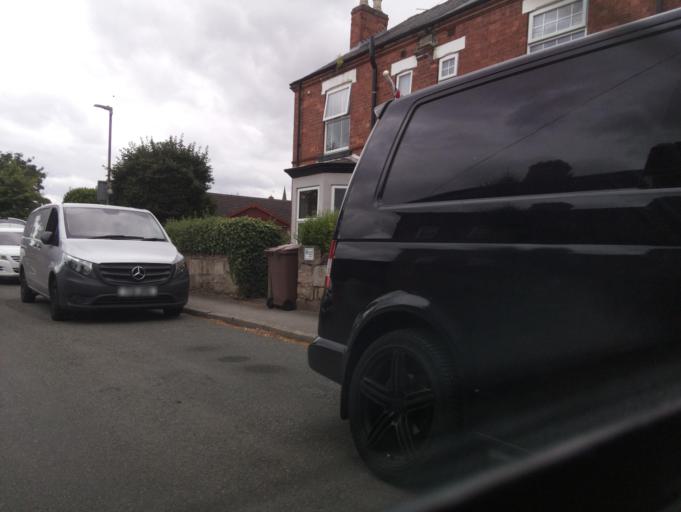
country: GB
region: England
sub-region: Derbyshire
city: Long Eaton
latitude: 52.8988
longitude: -1.3161
